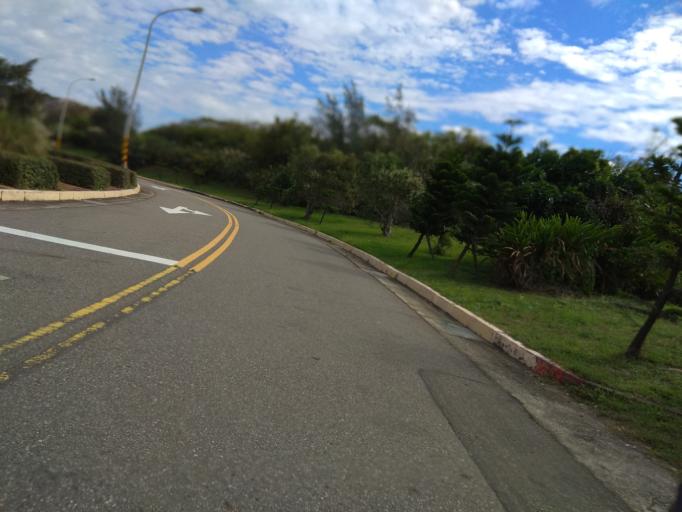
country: TW
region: Taiwan
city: Taoyuan City
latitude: 25.0438
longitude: 121.0851
